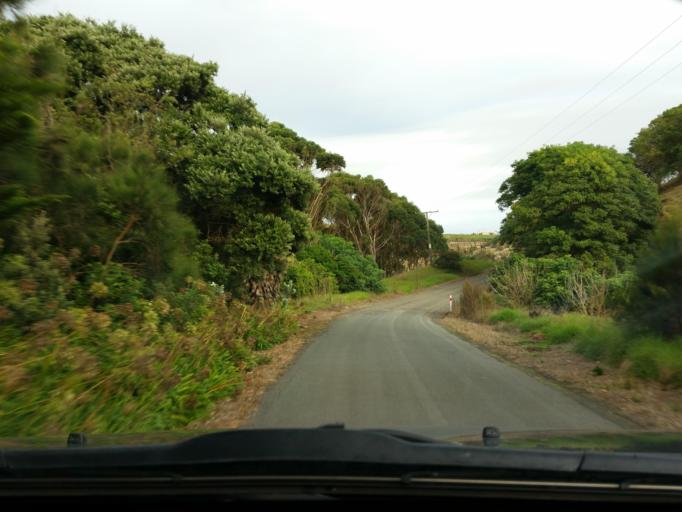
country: NZ
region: Northland
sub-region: Kaipara District
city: Dargaville
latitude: -35.8757
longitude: 173.6914
